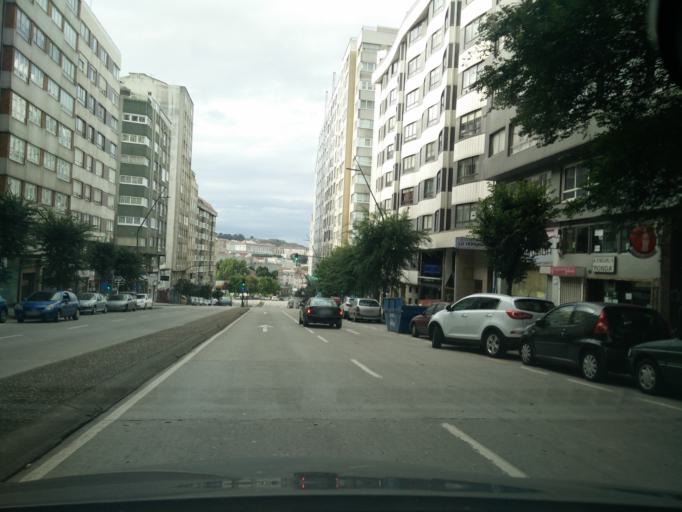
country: ES
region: Galicia
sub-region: Provincia da Coruna
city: A Coruna
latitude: 43.3638
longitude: -8.4234
